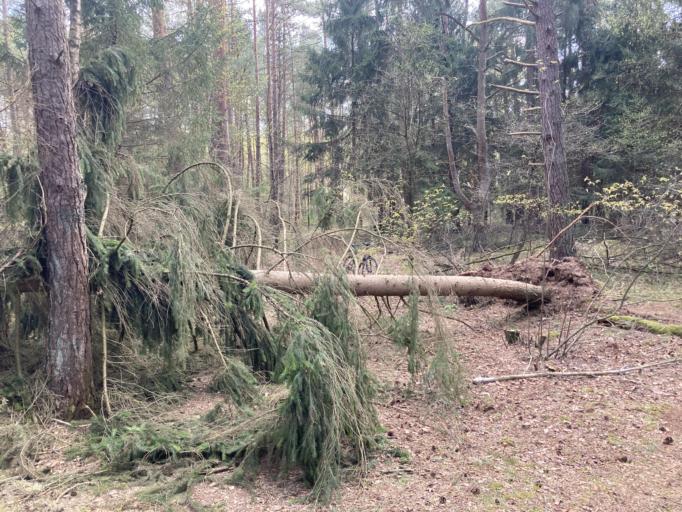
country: DE
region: Lower Saxony
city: Brietlingen
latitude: 53.3101
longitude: 10.4373
